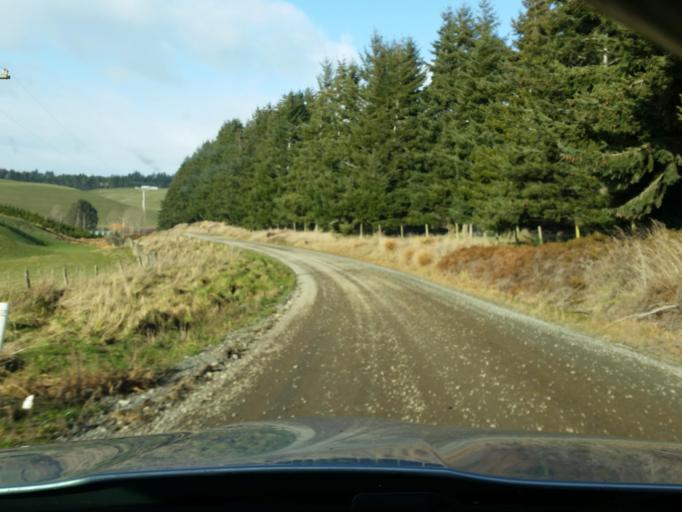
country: NZ
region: Southland
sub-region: Southland District
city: Te Anau
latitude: -45.4885
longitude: 167.8273
